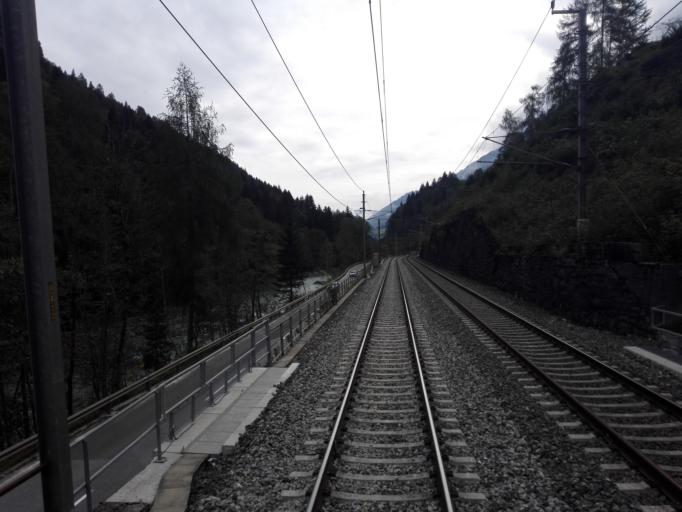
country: AT
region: Salzburg
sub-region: Politischer Bezirk Sankt Johann im Pongau
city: Goldegg
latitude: 47.2990
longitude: 13.0820
